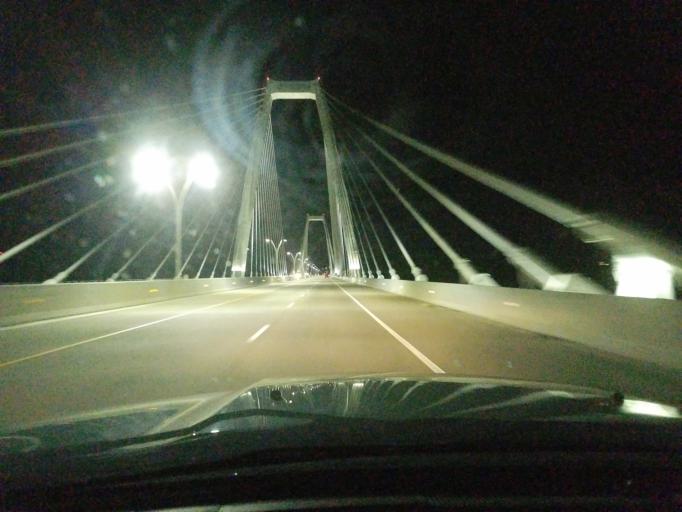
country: US
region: Kentucky
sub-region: Jefferson County
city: Prospect
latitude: 38.3403
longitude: -85.6404
